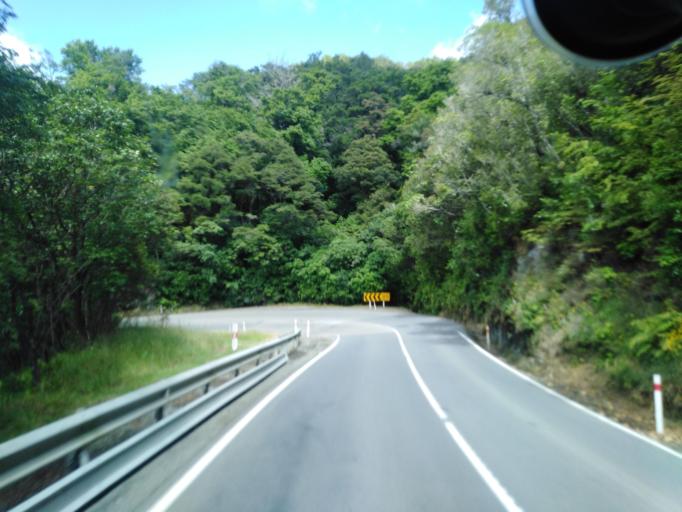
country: NZ
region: Nelson
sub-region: Nelson City
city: Nelson
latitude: -41.2228
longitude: 173.4356
